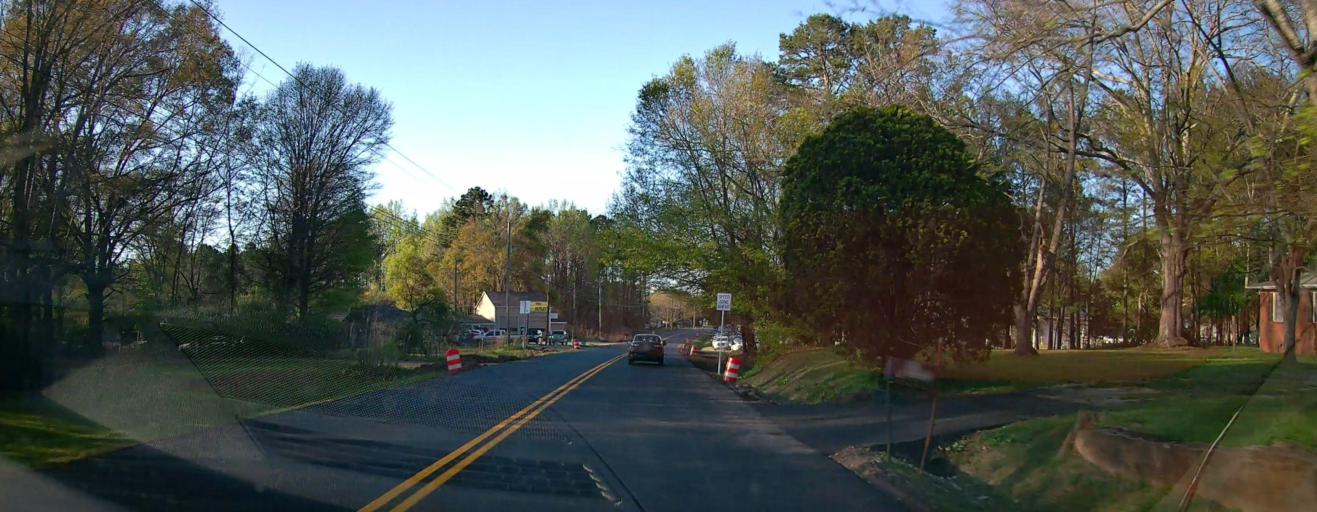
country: US
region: Georgia
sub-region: Newton County
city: Porterdale
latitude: 33.5564
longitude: -83.9062
